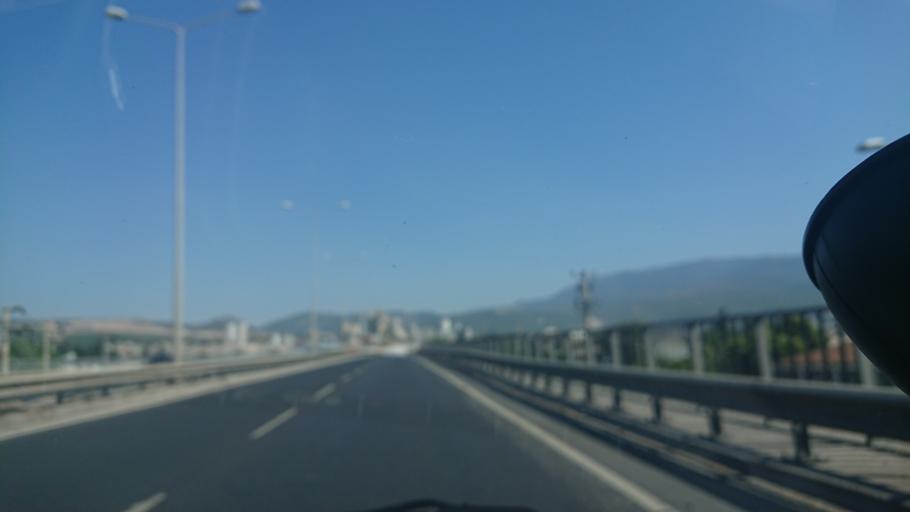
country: TR
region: Izmir
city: Bornova
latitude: 38.4578
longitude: 27.2496
